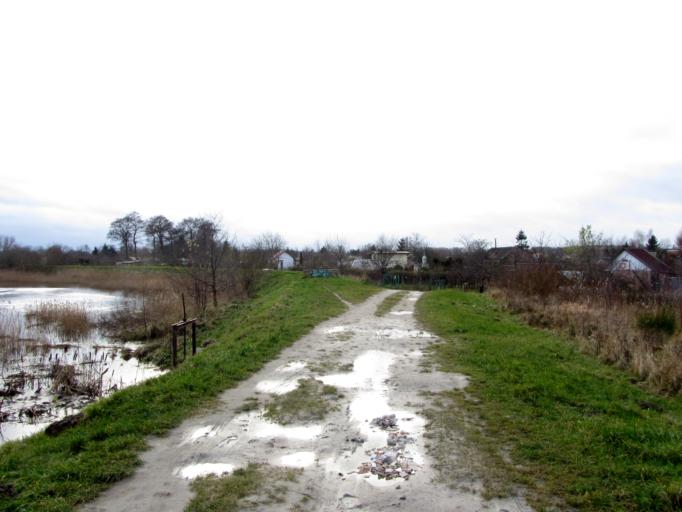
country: PL
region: West Pomeranian Voivodeship
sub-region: Powiat kolobrzeski
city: Kolobrzeg
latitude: 54.1673
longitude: 15.5771
